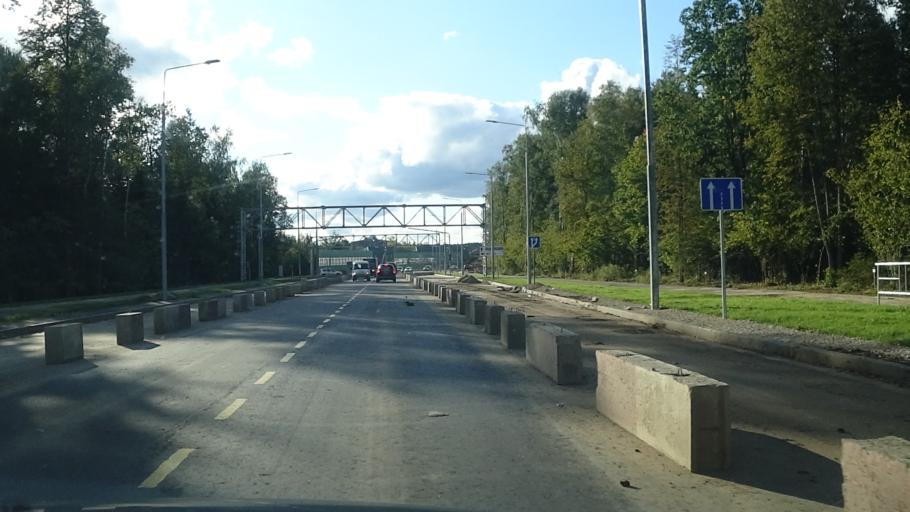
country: RU
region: Moskovskaya
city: Filimonki
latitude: 55.5687
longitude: 37.3997
